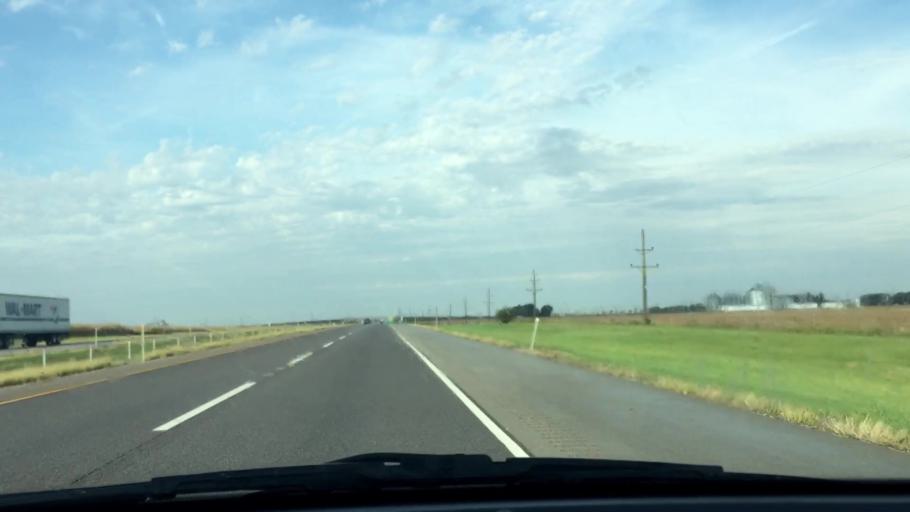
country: US
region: Illinois
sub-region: Lee County
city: Franklin Grove
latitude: 41.8229
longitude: -89.3733
